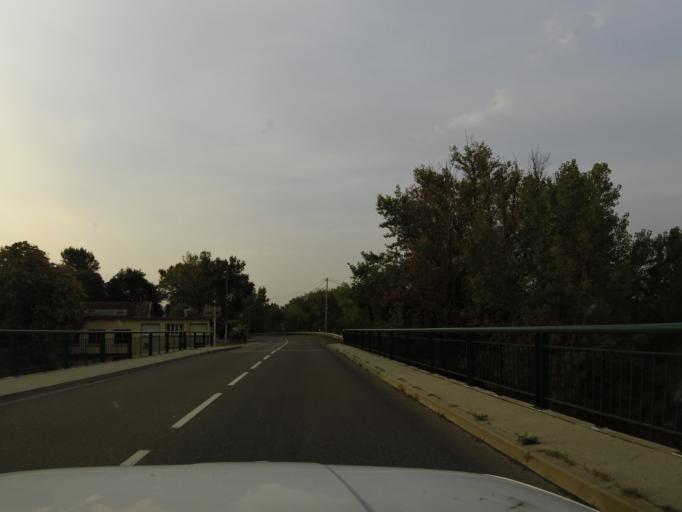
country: FR
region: Rhone-Alpes
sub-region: Departement de l'Ain
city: Saint-Jean-de-Niost
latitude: 45.8164
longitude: 5.2127
